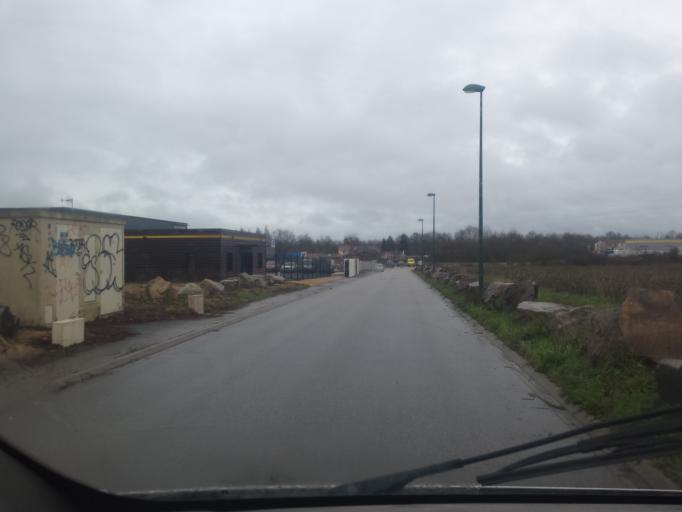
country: FR
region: Pays de la Loire
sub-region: Departement de la Vendee
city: La Roche-sur-Yon
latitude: 46.6397
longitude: -1.4091
